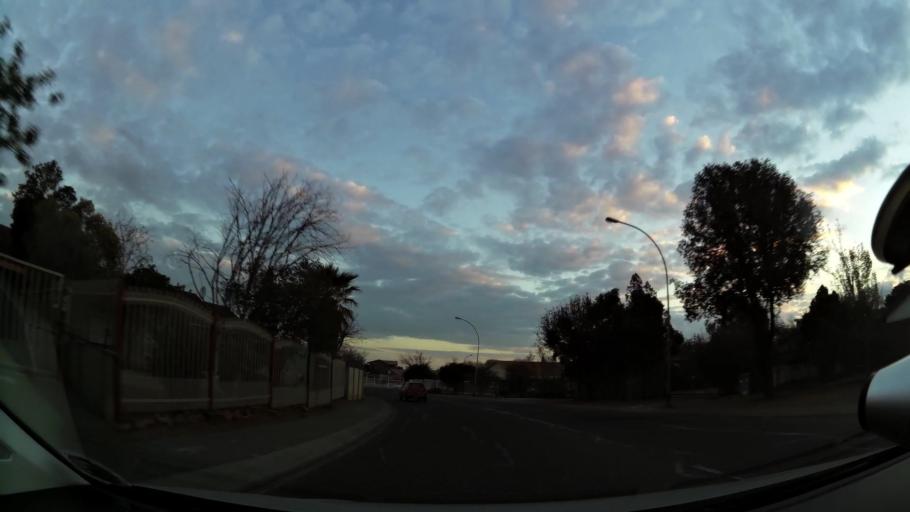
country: ZA
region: Orange Free State
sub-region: Mangaung Metropolitan Municipality
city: Bloemfontein
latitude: -29.1650
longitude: 26.1872
